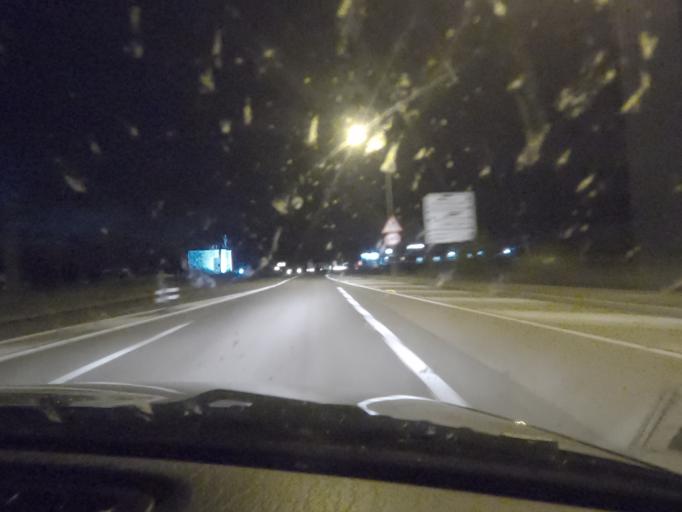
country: ES
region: Extremadura
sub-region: Provincia de Caceres
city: Moraleja
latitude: 40.0591
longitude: -6.6473
